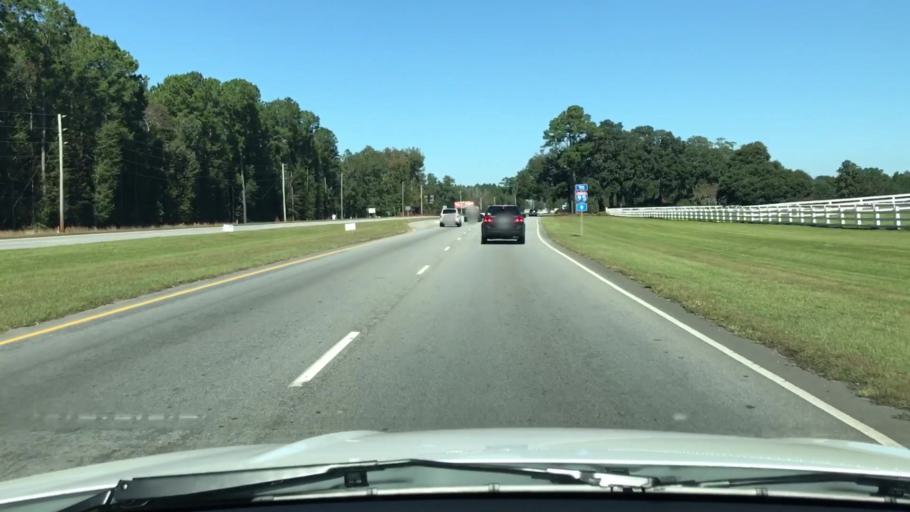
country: US
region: South Carolina
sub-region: Beaufort County
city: Bluffton
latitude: 32.3446
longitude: -80.9272
